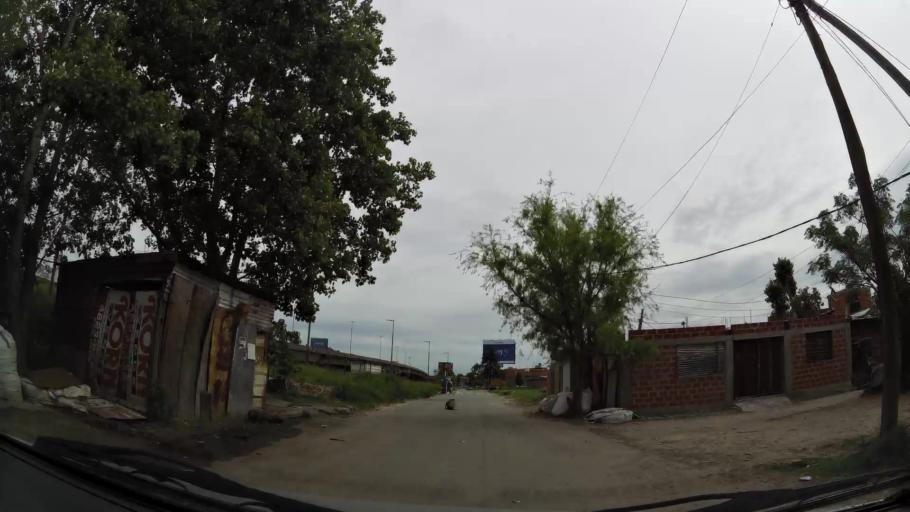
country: AR
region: Buenos Aires
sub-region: Partido de Avellaneda
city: Avellaneda
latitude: -34.6659
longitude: -58.3425
